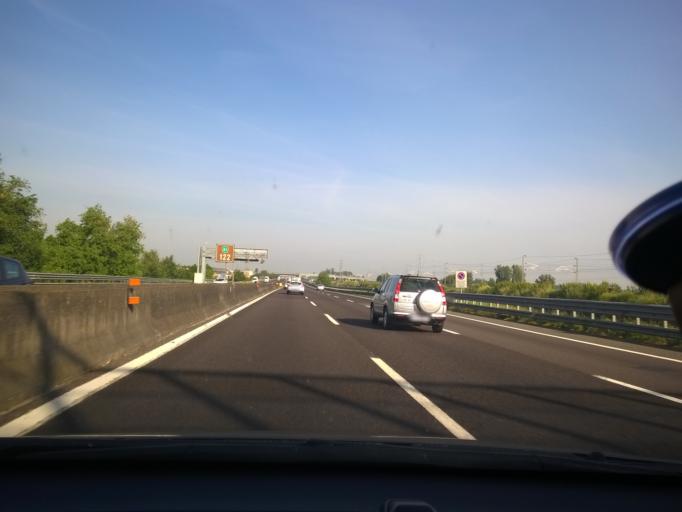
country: IT
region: Emilia-Romagna
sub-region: Provincia di Reggio Emilia
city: Praticello
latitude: 44.7919
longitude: 10.4693
